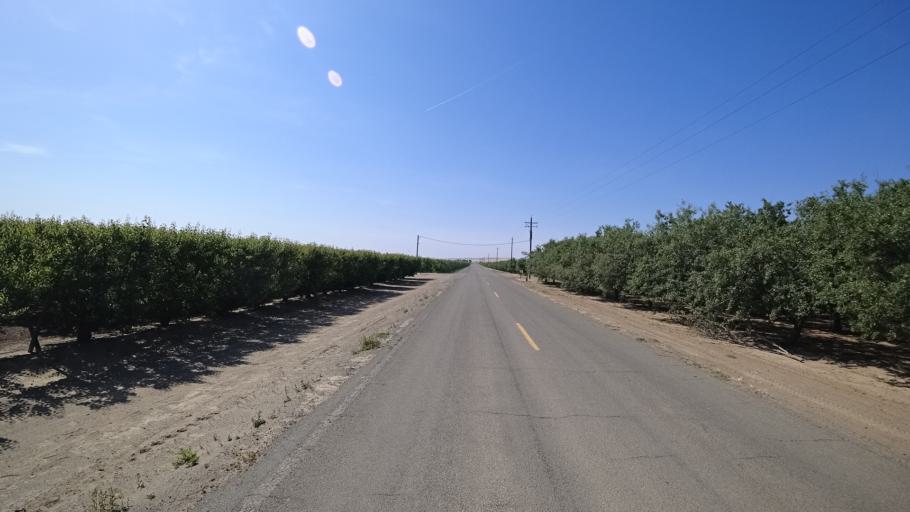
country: US
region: California
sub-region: Kings County
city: Kettleman City
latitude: 36.0588
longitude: -120.0036
